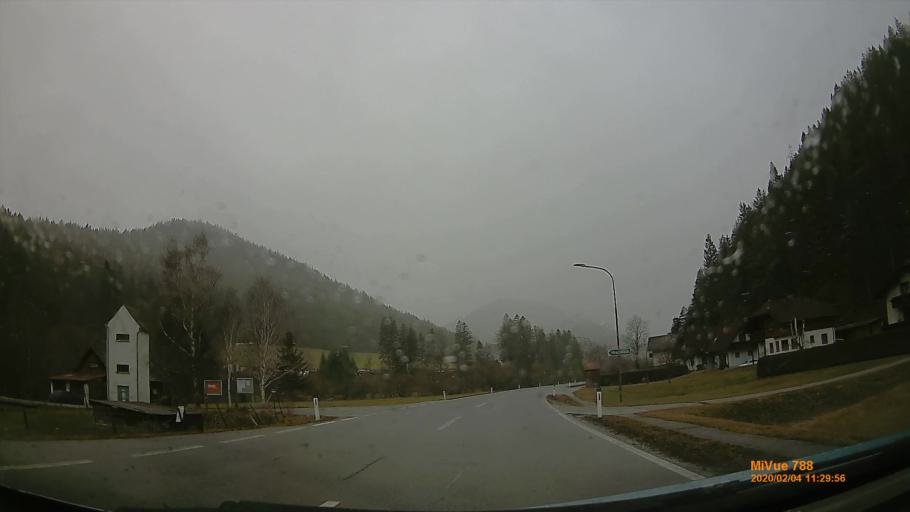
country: AT
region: Styria
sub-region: Politischer Bezirk Bruck-Muerzzuschlag
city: Kapellen
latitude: 47.6540
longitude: 15.6089
